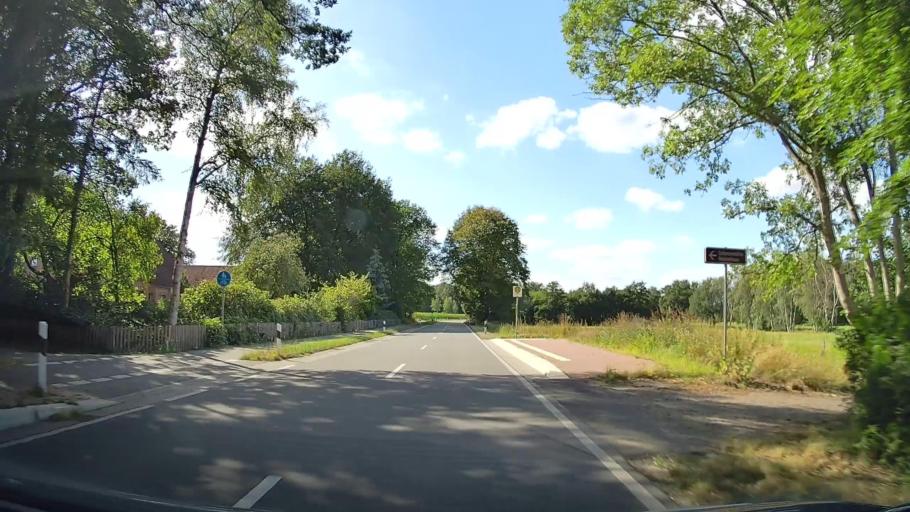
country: DE
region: Lower Saxony
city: Loningen
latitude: 52.7061
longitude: 7.7549
